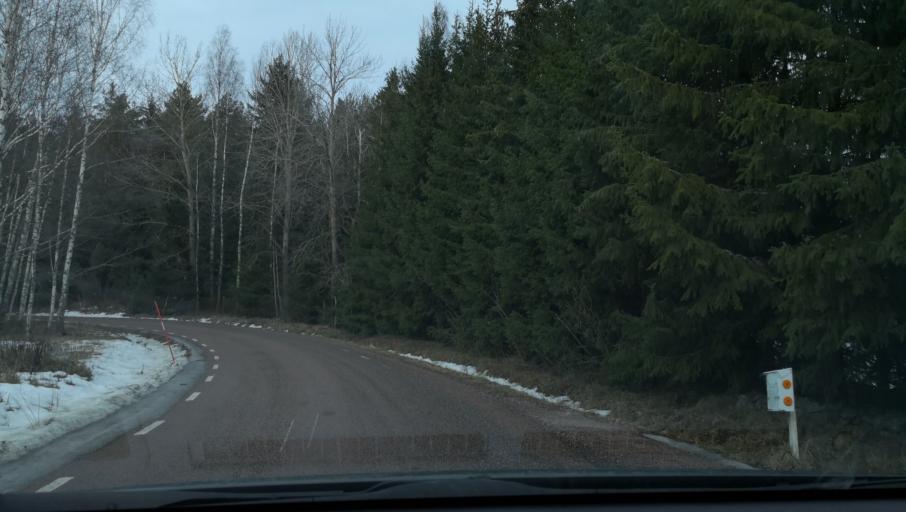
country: SE
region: Vaestmanland
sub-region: Vasteras
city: Skultuna
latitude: 59.6271
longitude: 16.4139
